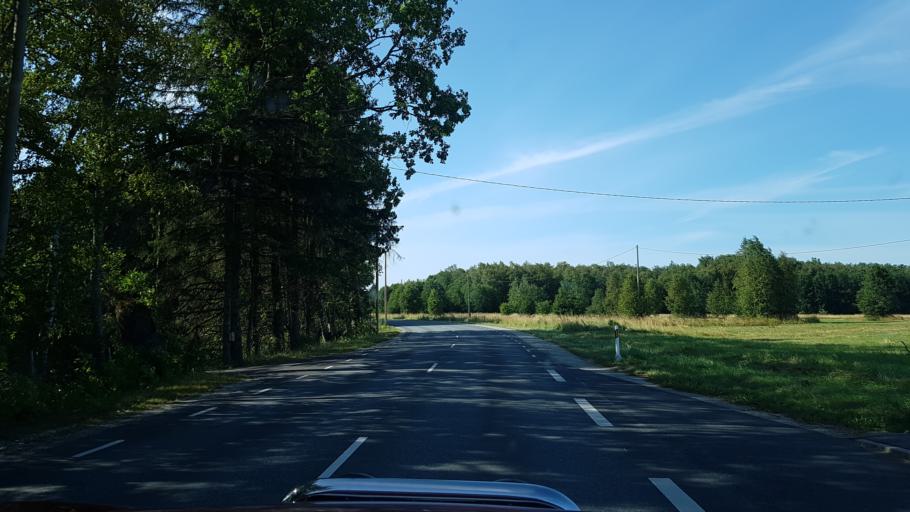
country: EE
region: Harju
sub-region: Rae vald
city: Jueri
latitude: 59.3819
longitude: 24.9280
